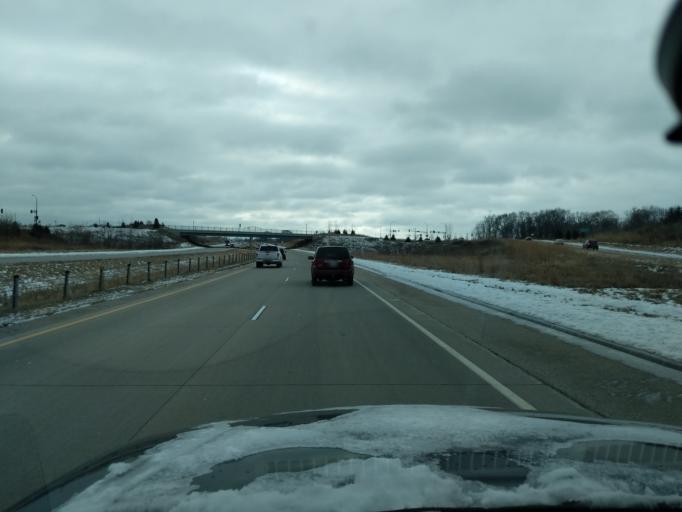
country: US
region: Minnesota
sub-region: Carver County
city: Chaska
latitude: 44.8081
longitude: -93.6236
